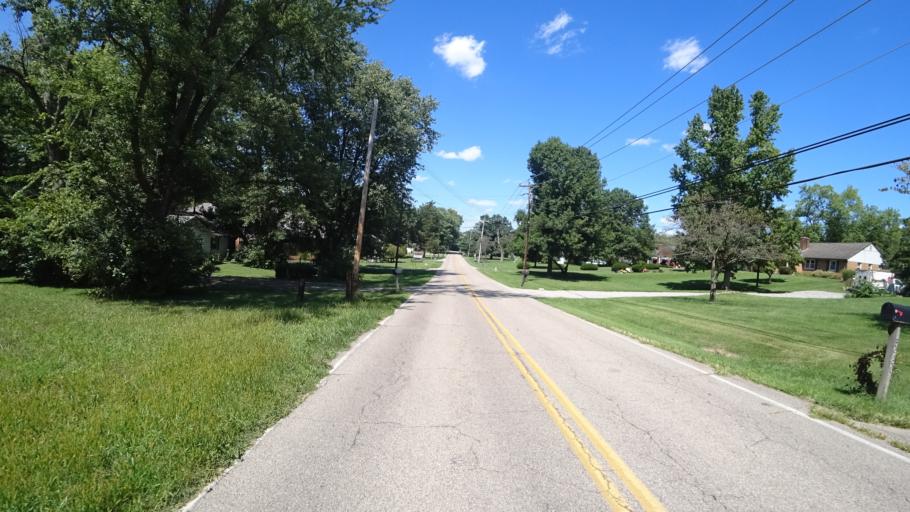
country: US
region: Ohio
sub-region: Butler County
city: New Miami
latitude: 39.4095
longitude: -84.5271
